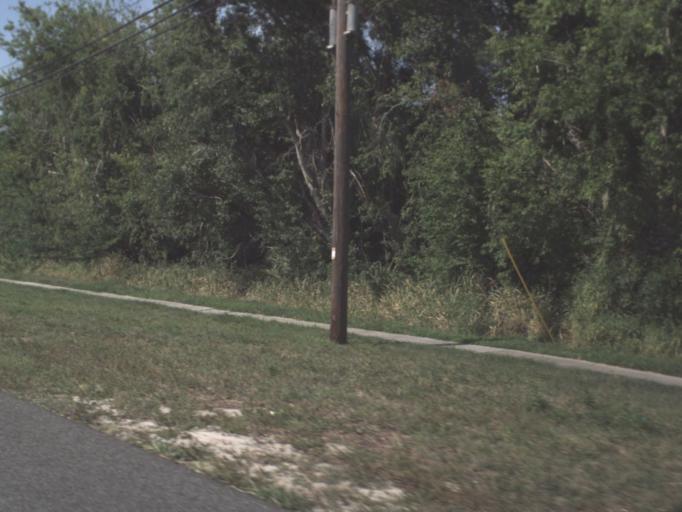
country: US
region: Florida
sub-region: Brevard County
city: Sharpes
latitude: 28.4336
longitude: -80.7604
